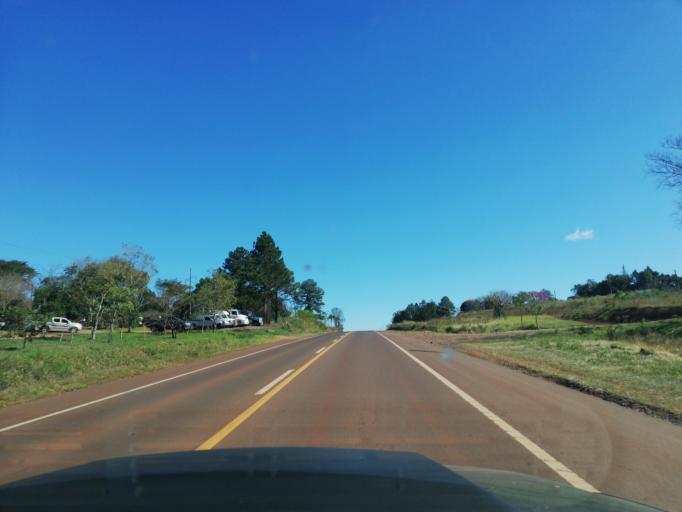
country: AR
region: Misiones
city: Aristobulo del Valle
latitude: -27.0935
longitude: -54.8680
